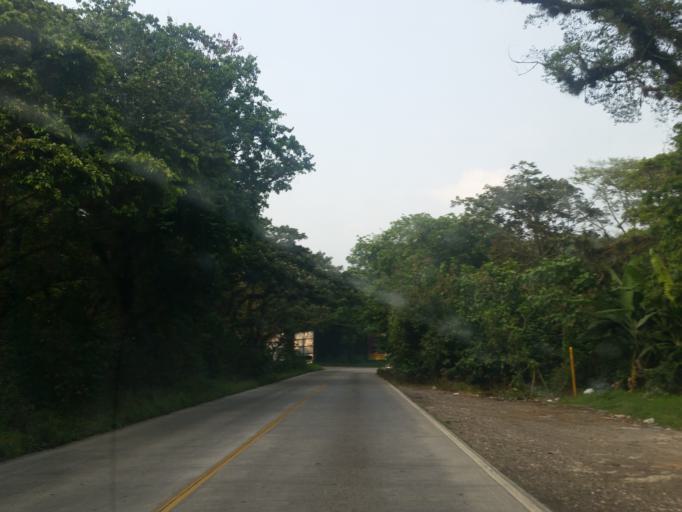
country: MX
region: Veracruz
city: Coatepec
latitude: 19.4305
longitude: -96.9600
